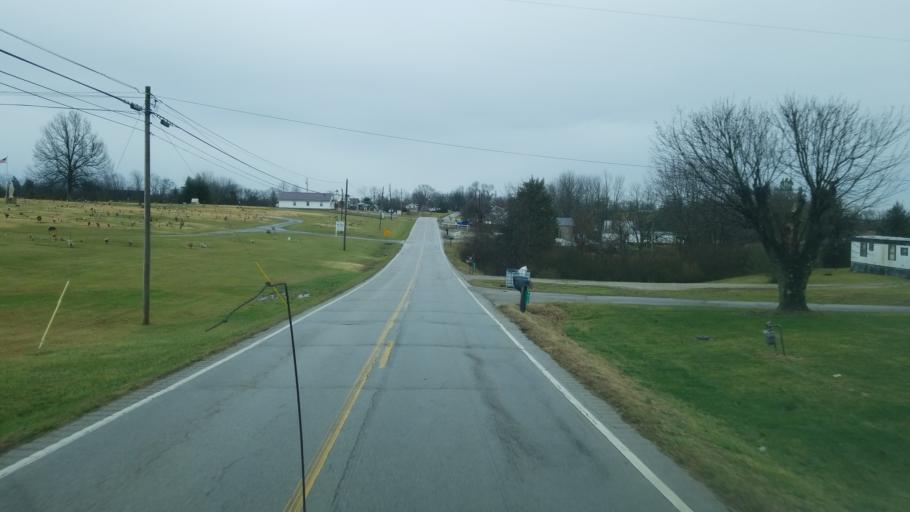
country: US
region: Kentucky
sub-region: Mason County
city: Maysville
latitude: 38.5893
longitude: -83.6648
